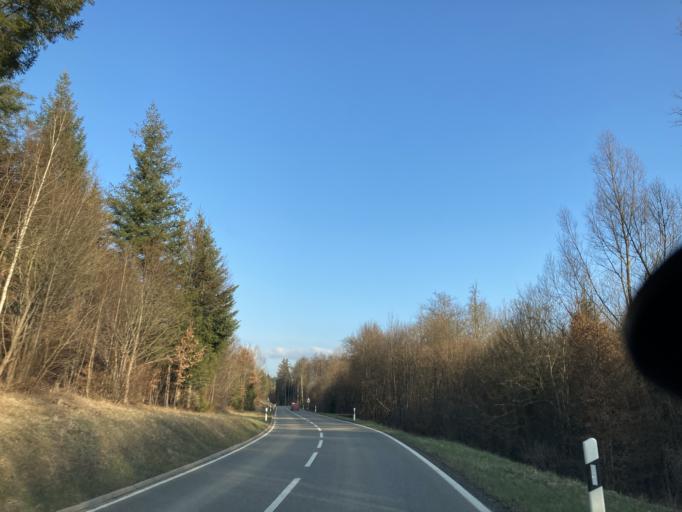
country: DE
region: Baden-Wuerttemberg
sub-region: Tuebingen Region
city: Bodelshausen
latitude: 48.4221
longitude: 8.9909
